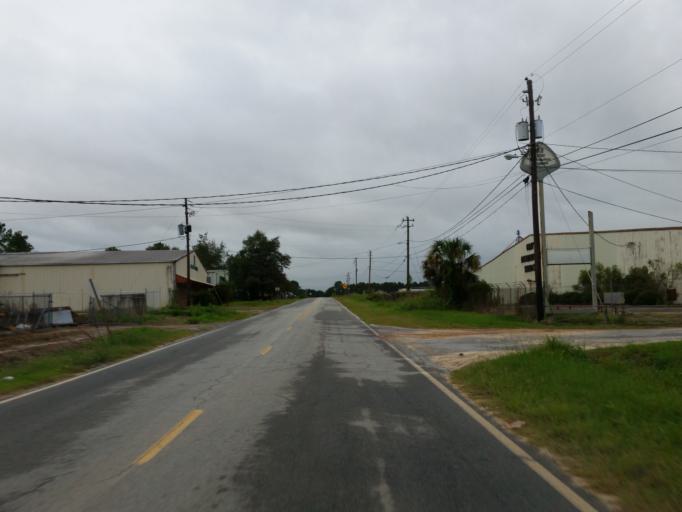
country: US
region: Georgia
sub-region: Turner County
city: Ashburn
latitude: 31.6791
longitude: -83.6371
